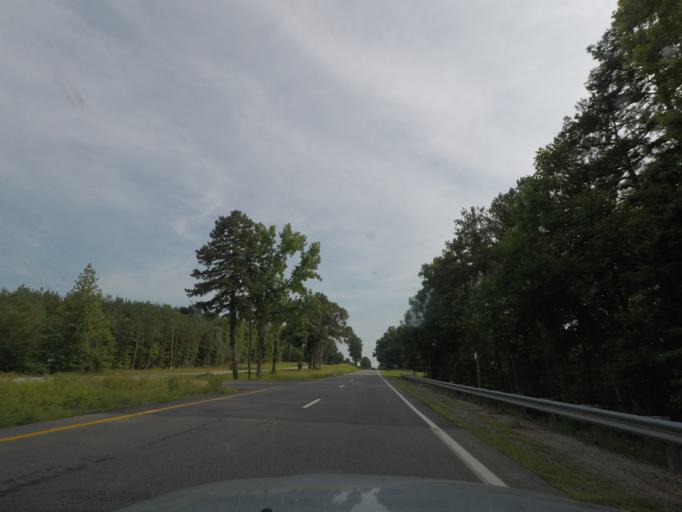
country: US
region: Virginia
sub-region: Mecklenburg County
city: Chase City
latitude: 36.9603
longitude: -78.4959
